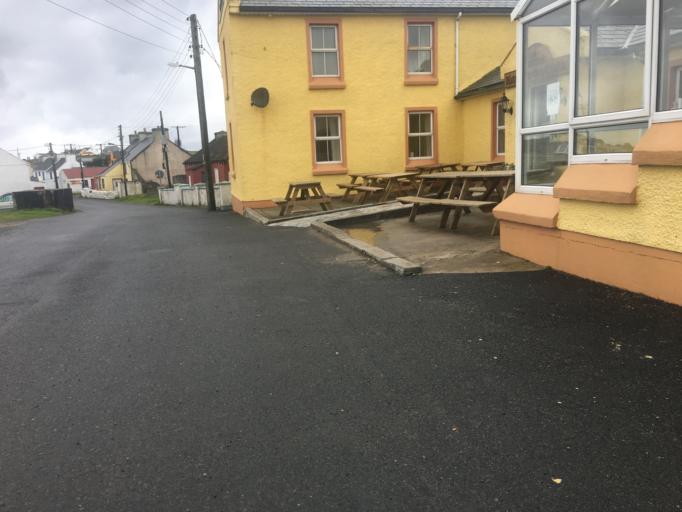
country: IE
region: Ulster
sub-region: County Donegal
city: Derrybeg
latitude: 55.2652
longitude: -8.2260
